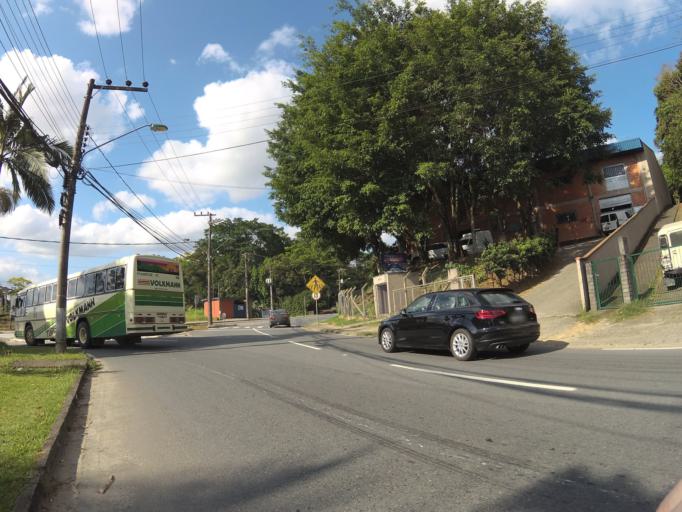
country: BR
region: Santa Catarina
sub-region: Blumenau
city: Blumenau
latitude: -26.8983
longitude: -49.1349
